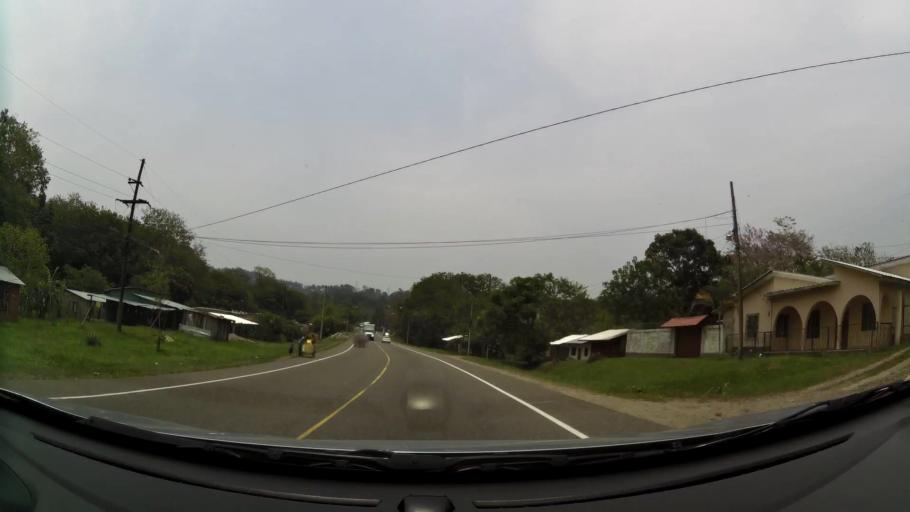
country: HN
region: Cortes
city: La Guama
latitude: 14.8817
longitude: -87.9383
